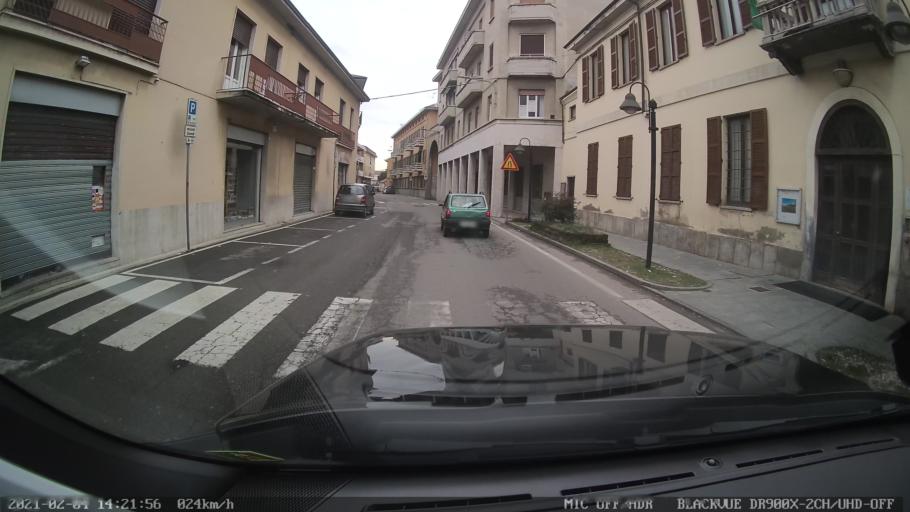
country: IT
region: Lombardy
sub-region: Provincia di Varese
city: Cairate
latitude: 45.6909
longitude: 8.8722
